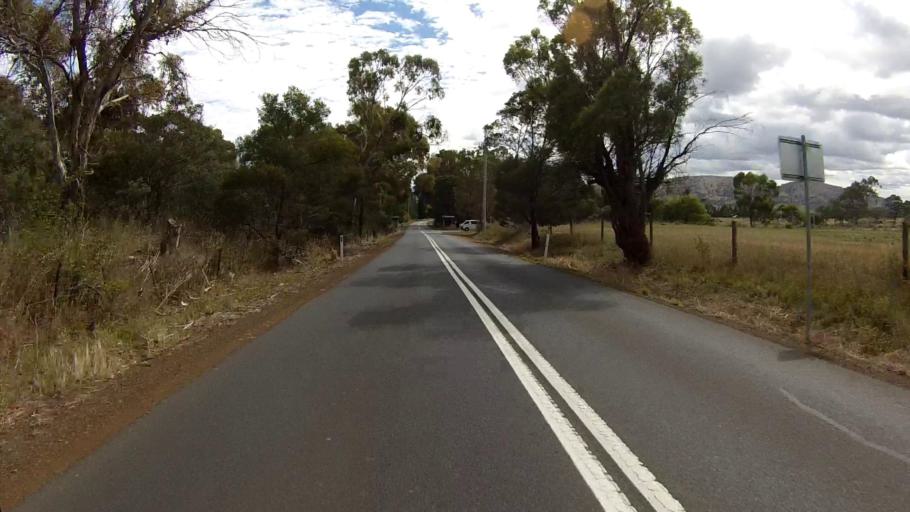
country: AU
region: Tasmania
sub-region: Clarence
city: Lindisfarne
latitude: -42.7660
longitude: 147.3922
